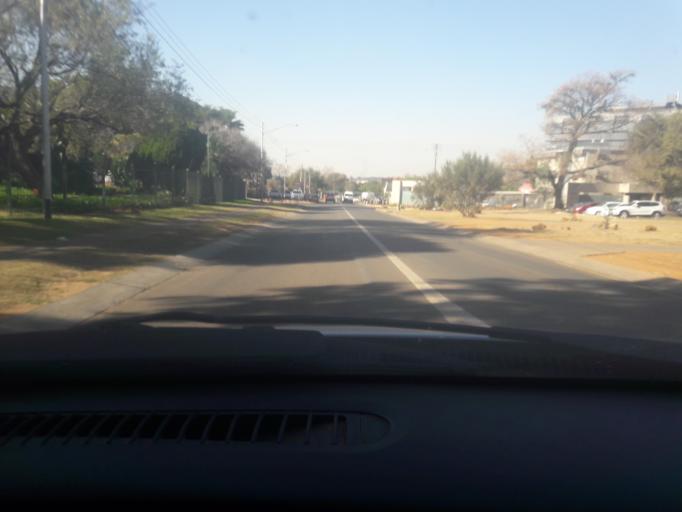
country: ZA
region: Gauteng
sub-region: City of Tshwane Metropolitan Municipality
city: Pretoria
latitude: -25.7684
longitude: 28.2659
